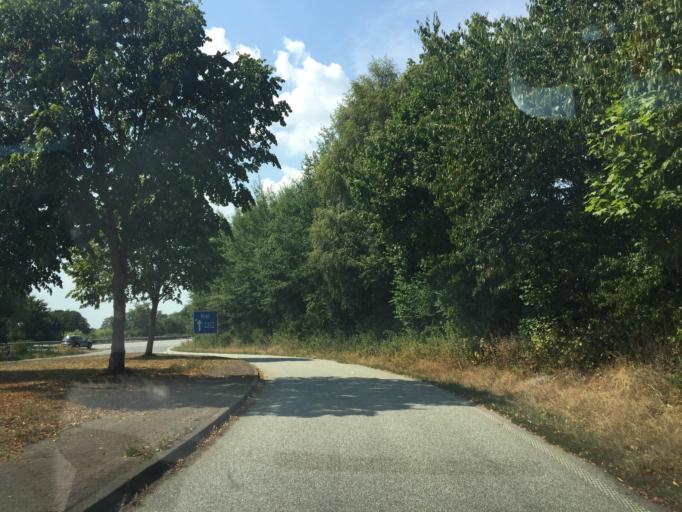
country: DE
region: Schleswig-Holstein
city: Bebensee
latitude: 53.8911
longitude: 10.2916
